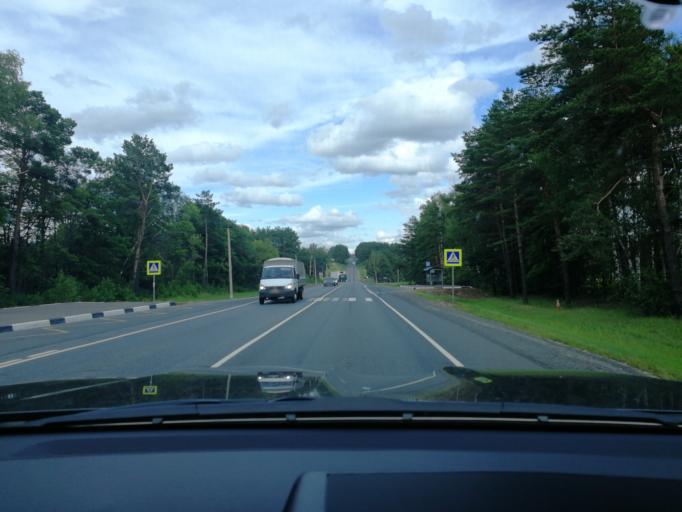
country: RU
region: Moskovskaya
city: Mikhnevo
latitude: 55.0720
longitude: 37.8226
